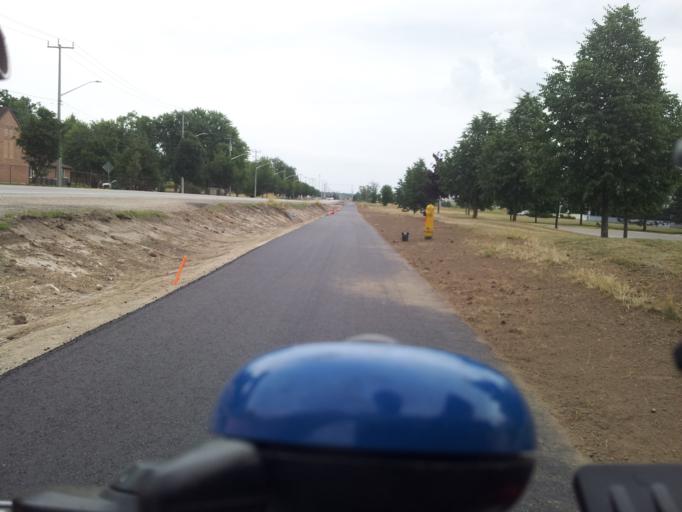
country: CA
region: Ontario
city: Stratford
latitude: 43.3603
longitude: -81.0062
